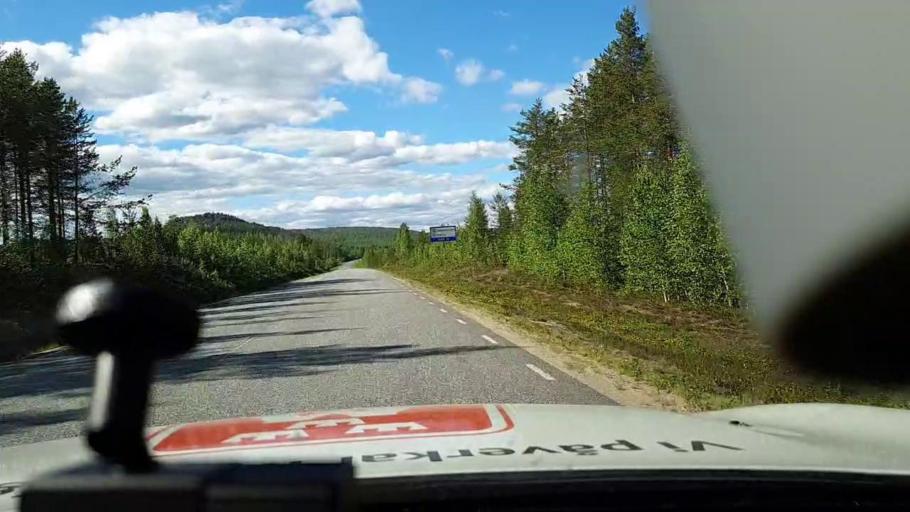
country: FI
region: Lapland
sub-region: Torniolaakso
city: Ylitornio
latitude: 66.2984
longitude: 23.6349
